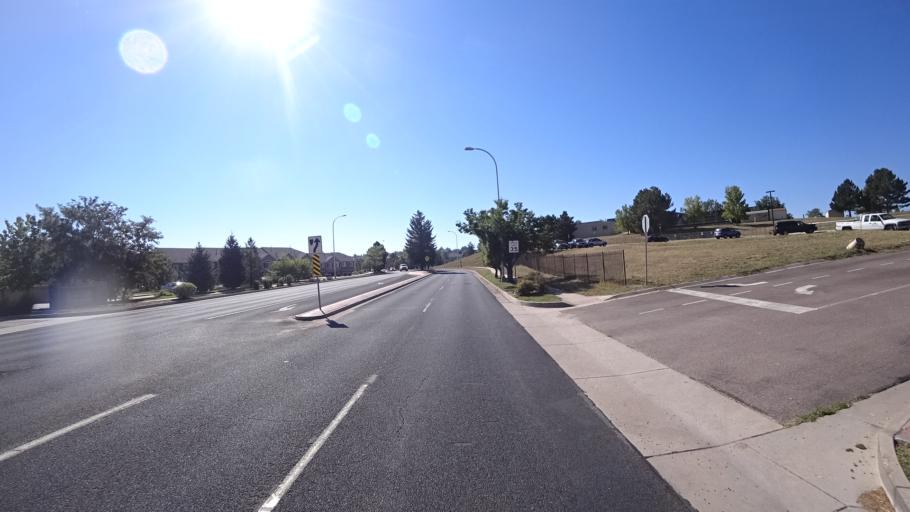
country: US
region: Colorado
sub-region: El Paso County
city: Cimarron Hills
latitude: 38.9248
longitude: -104.7501
